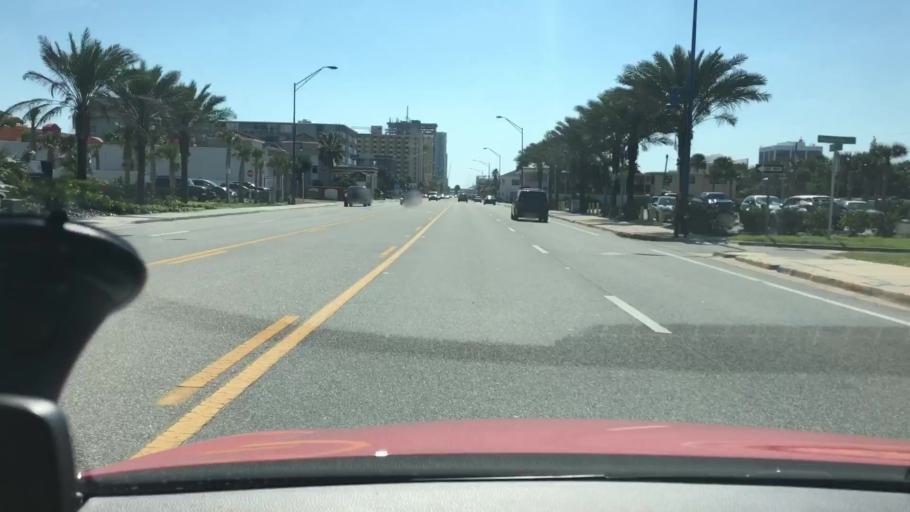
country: US
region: Florida
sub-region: Volusia County
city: Holly Hill
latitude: 29.2407
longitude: -81.0150
